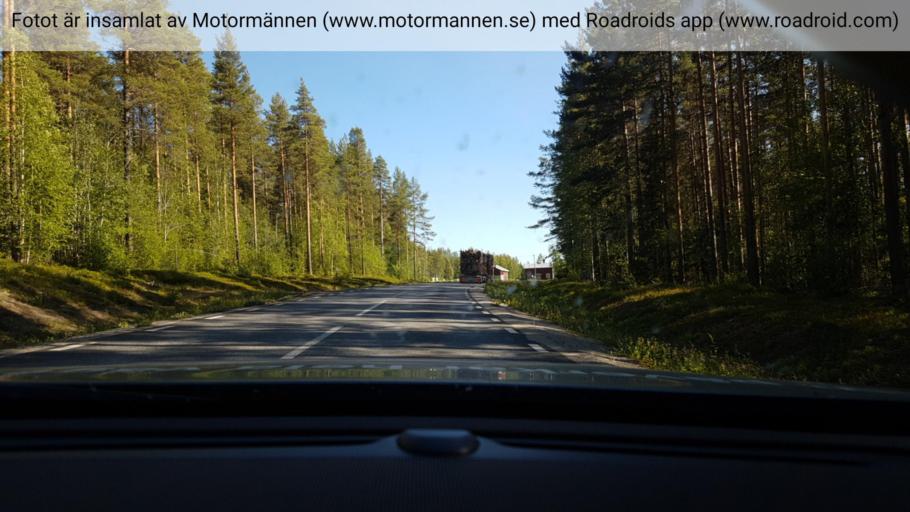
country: SE
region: Vaesterbotten
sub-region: Bjurholms Kommun
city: Bjurholm
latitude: 64.3480
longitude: 19.1493
